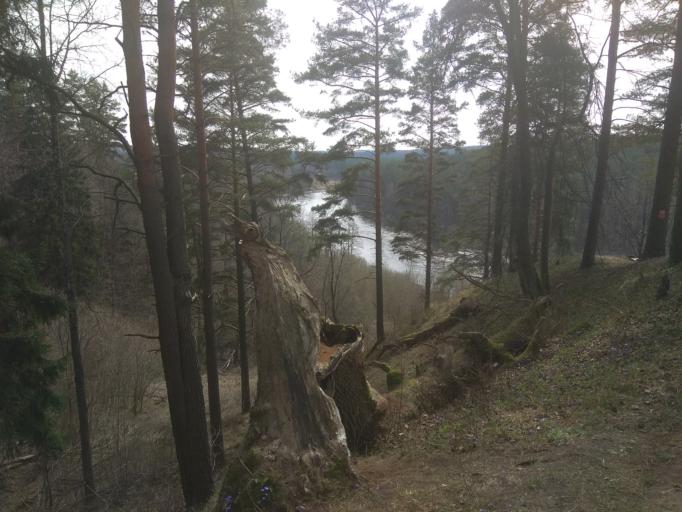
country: LT
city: Grigiskes
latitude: 54.7390
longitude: 25.0222
